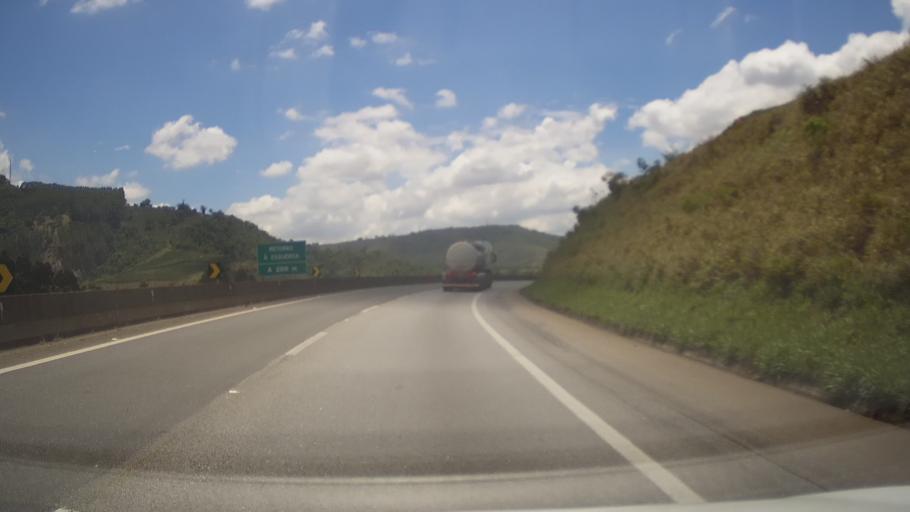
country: BR
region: Minas Gerais
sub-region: Campanha
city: Campanha
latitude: -21.8111
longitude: -45.4888
